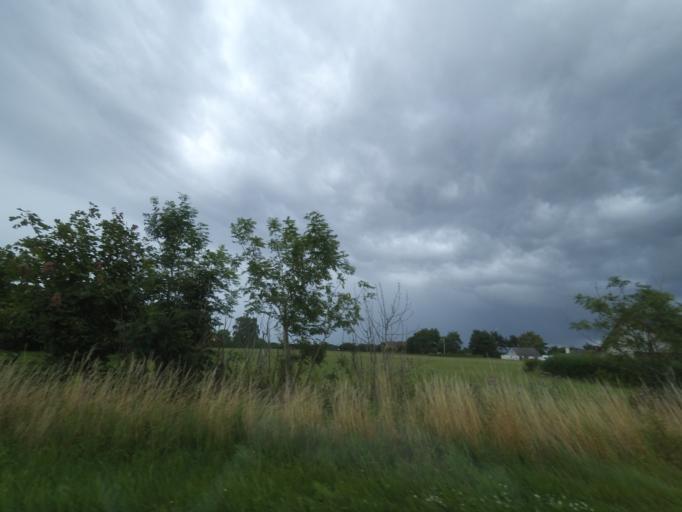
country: DK
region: South Denmark
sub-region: Middelfart Kommune
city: Norre Aby
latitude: 55.4657
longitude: 9.9119
